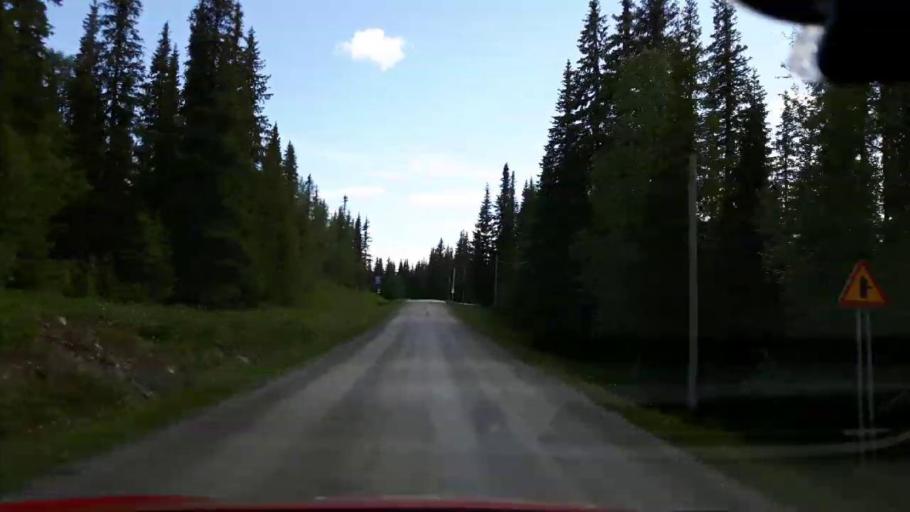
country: SE
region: Jaemtland
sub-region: Krokoms Kommun
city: Valla
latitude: 63.7802
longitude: 14.0446
